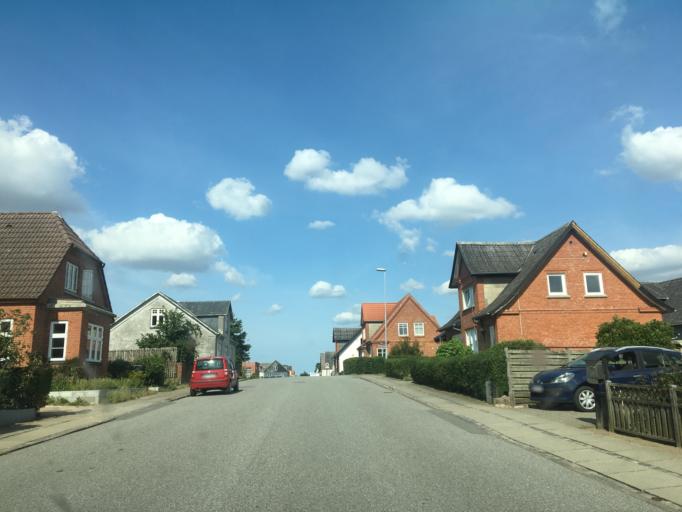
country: DK
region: South Denmark
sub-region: Middelfart Kommune
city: Ejby
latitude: 55.3957
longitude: 9.9693
